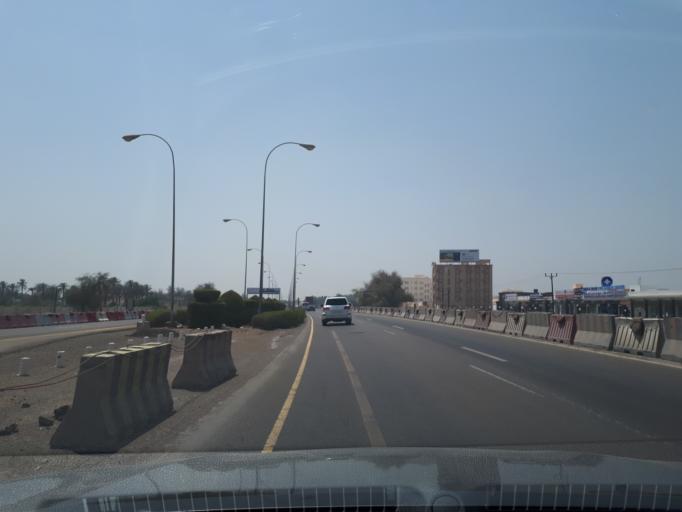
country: OM
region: Al Batinah
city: Al Sohar
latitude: 24.3894
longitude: 56.6981
